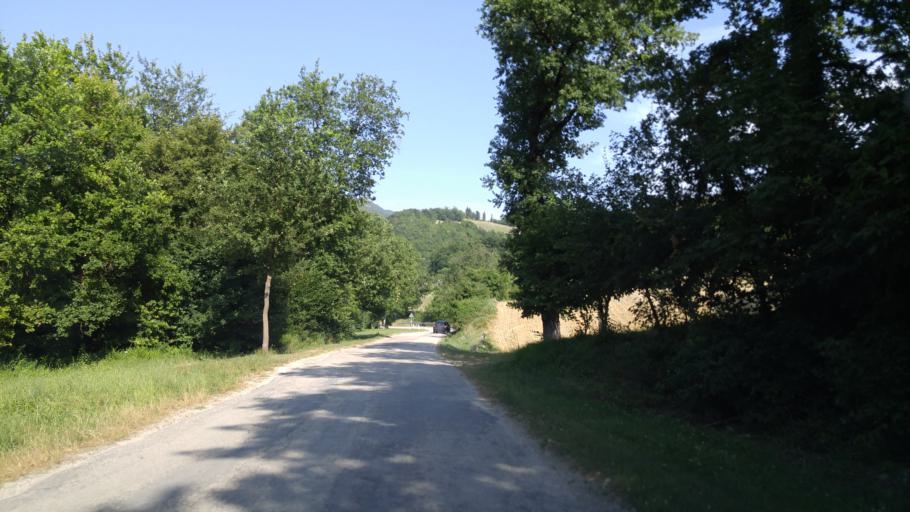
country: IT
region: The Marches
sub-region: Provincia di Pesaro e Urbino
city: Acqualagna
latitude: 43.6339
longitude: 12.6999
